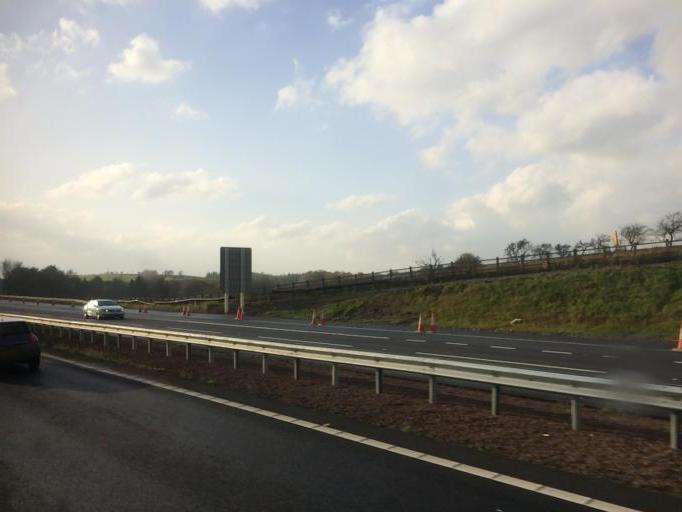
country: GB
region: Scotland
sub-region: North Lanarkshire
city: Newarthill
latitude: 55.8408
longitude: -3.9090
